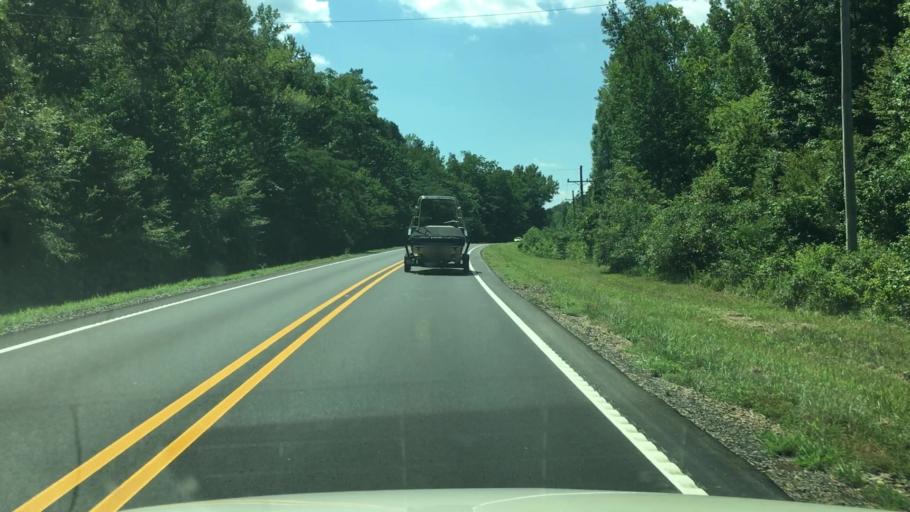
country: US
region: Arkansas
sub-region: Garland County
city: Rockwell
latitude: 34.5166
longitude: -93.2983
